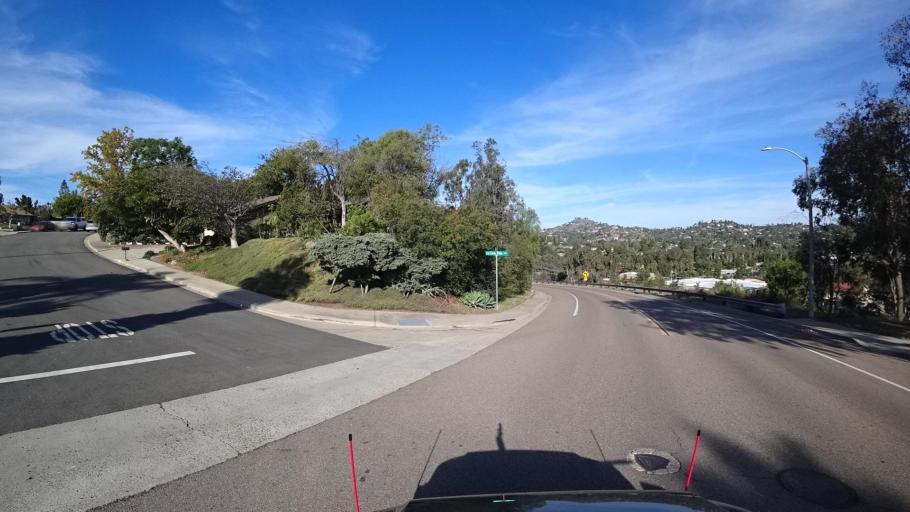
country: US
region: California
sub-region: San Diego County
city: Casa de Oro-Mount Helix
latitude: 32.7439
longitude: -116.9607
